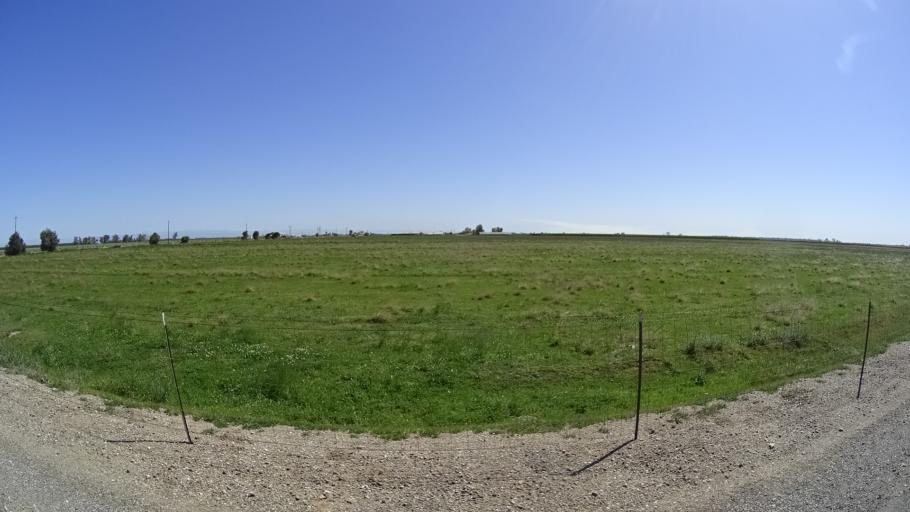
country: US
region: California
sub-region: Glenn County
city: Willows
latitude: 39.6310
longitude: -122.2535
